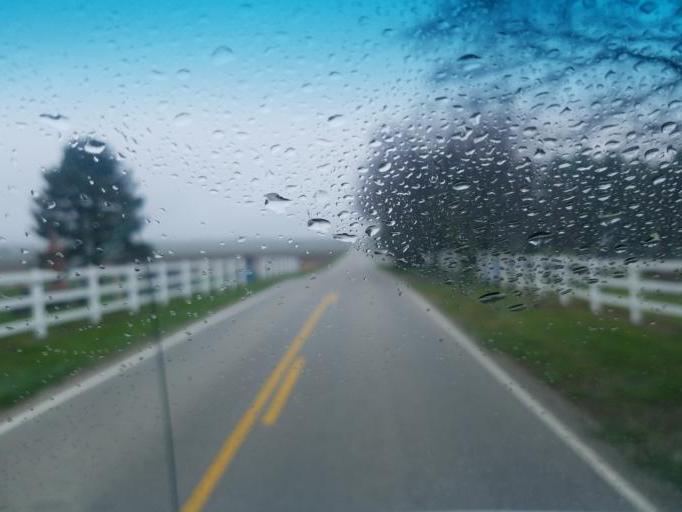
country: US
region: Ohio
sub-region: Wood County
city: North Baltimore
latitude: 41.1429
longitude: -83.6312
